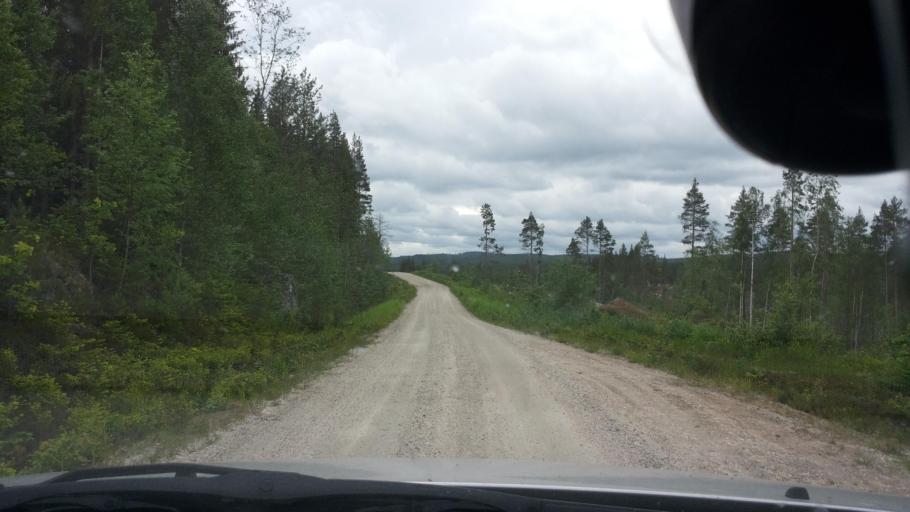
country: SE
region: Gaevleborg
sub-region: Ovanakers Kommun
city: Edsbyn
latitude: 61.4788
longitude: 15.3111
